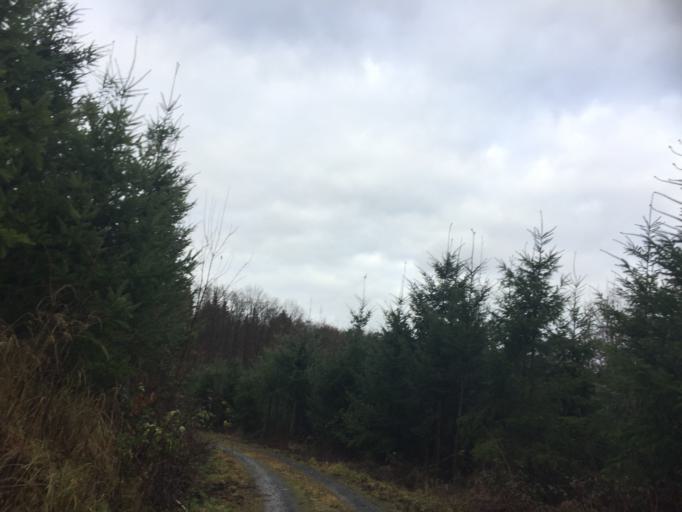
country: DE
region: Hesse
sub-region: Regierungsbezirk Giessen
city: Lich
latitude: 50.5361
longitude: 8.7942
